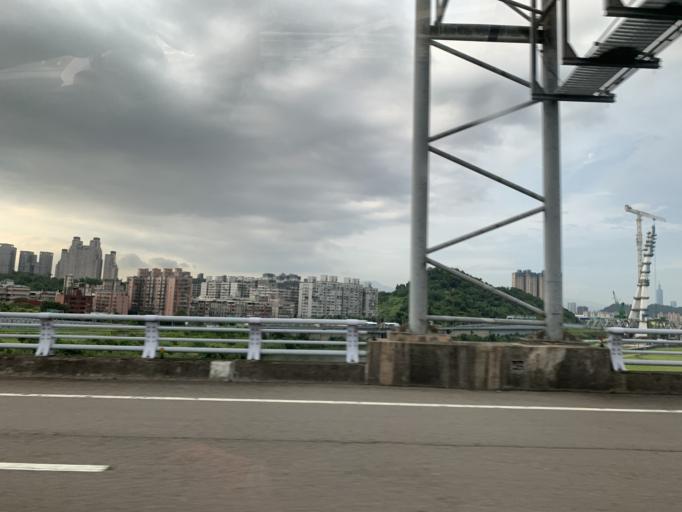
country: TW
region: Taipei
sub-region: Taipei
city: Banqiao
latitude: 24.9808
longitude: 121.5212
